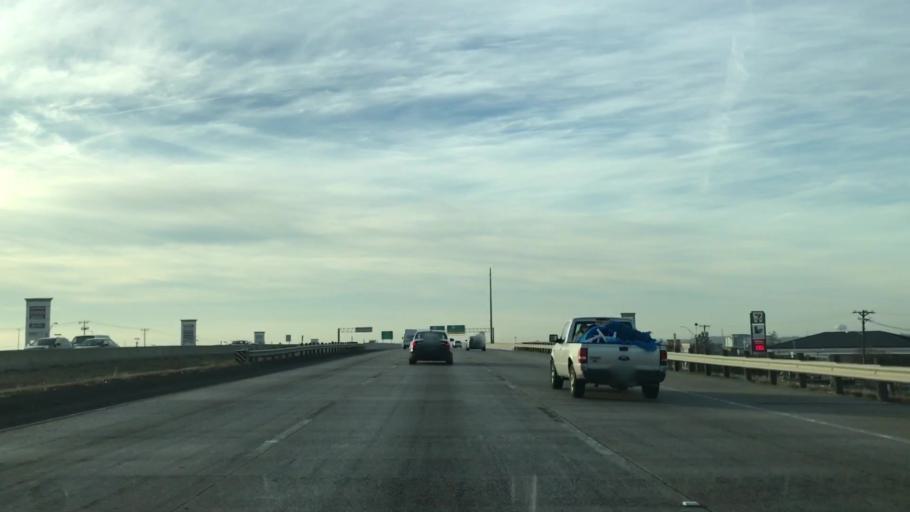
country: US
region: Texas
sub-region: Tarrant County
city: Euless
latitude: 32.8825
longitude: -97.0994
